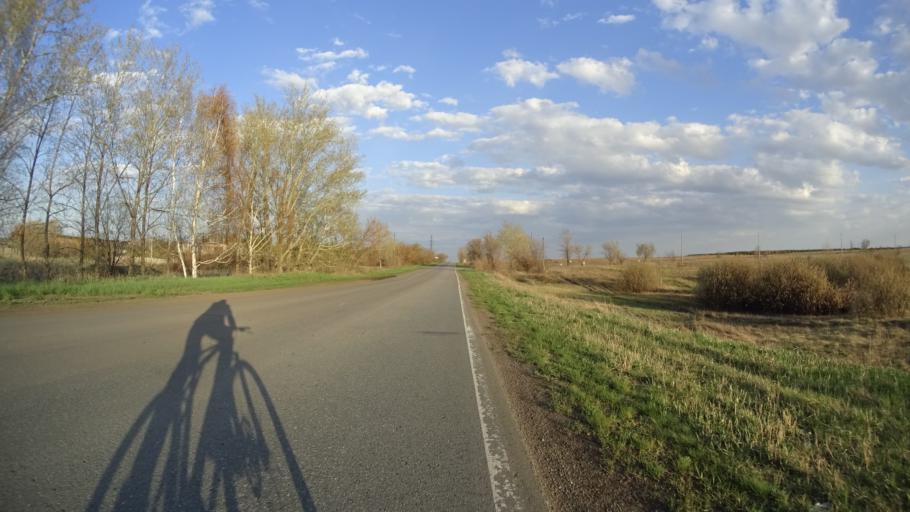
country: RU
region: Chelyabinsk
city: Troitsk
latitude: 54.0553
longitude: 61.5873
